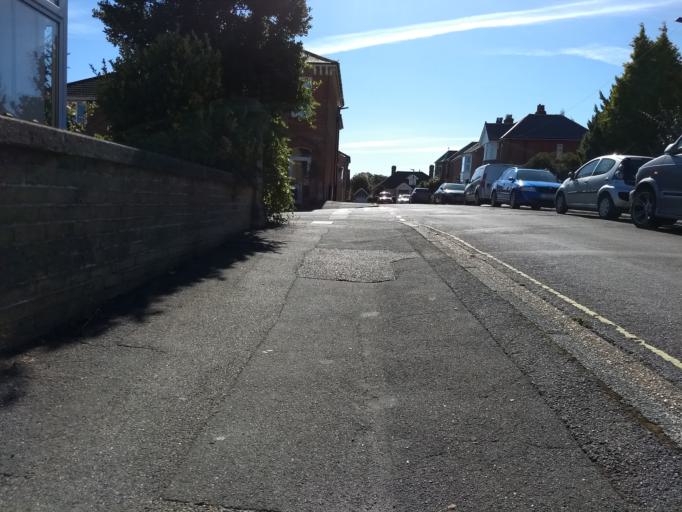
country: GB
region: England
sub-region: Isle of Wight
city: Newport
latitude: 50.6946
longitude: -1.2942
